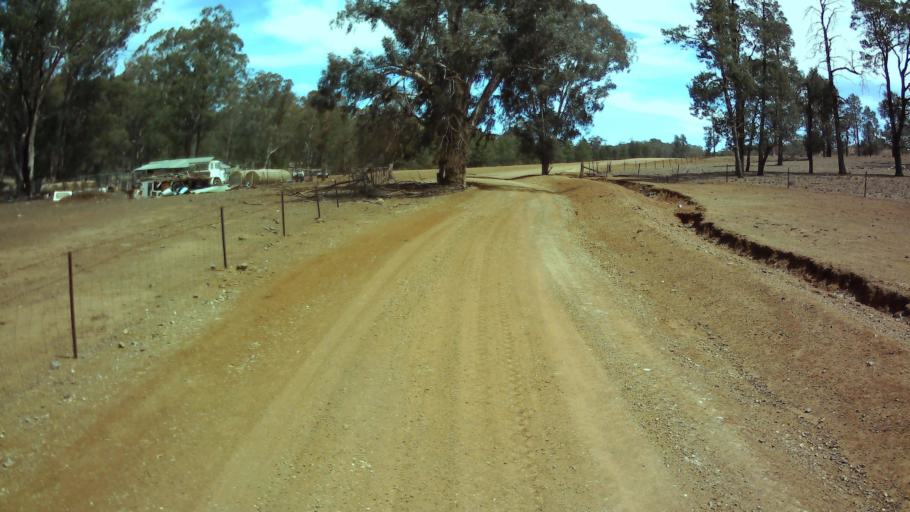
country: AU
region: New South Wales
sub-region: Weddin
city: Grenfell
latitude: -33.7933
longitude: 148.1602
